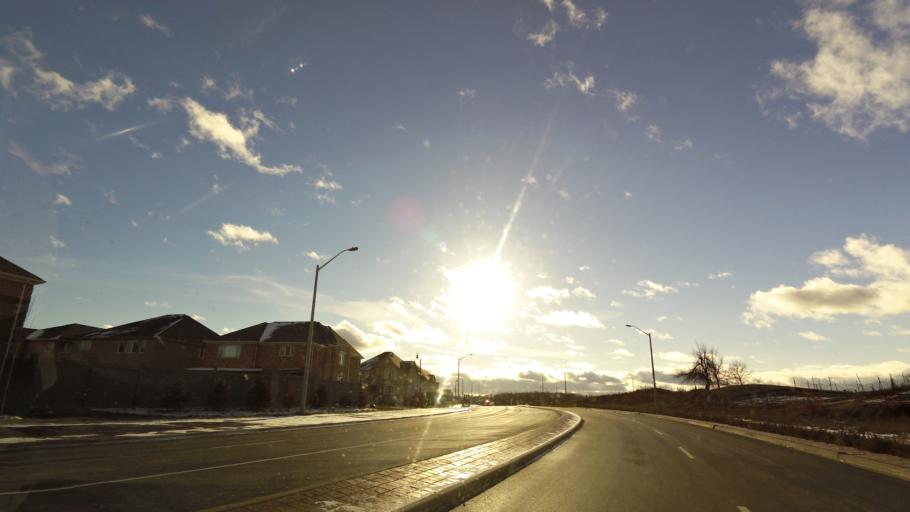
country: CA
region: Ontario
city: Brampton
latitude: 43.6373
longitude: -79.7843
